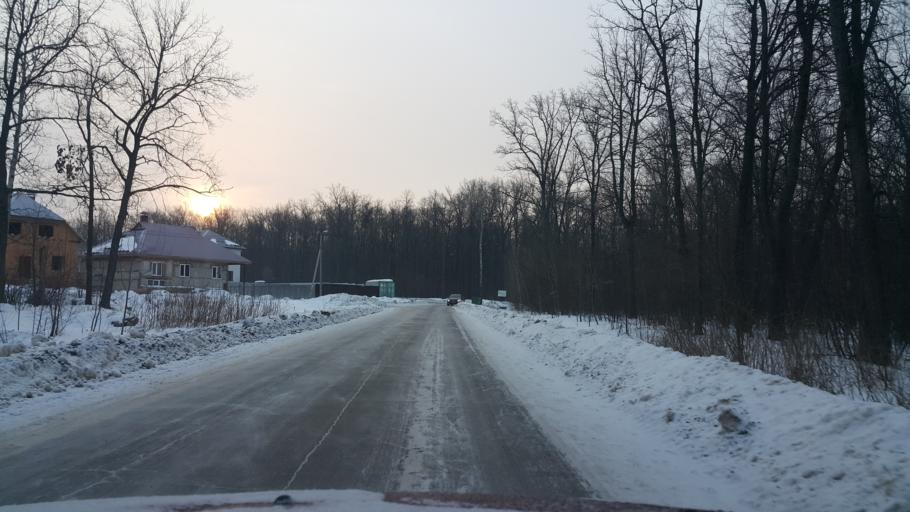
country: RU
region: Tambov
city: Kotovsk
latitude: 52.5726
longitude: 41.5210
